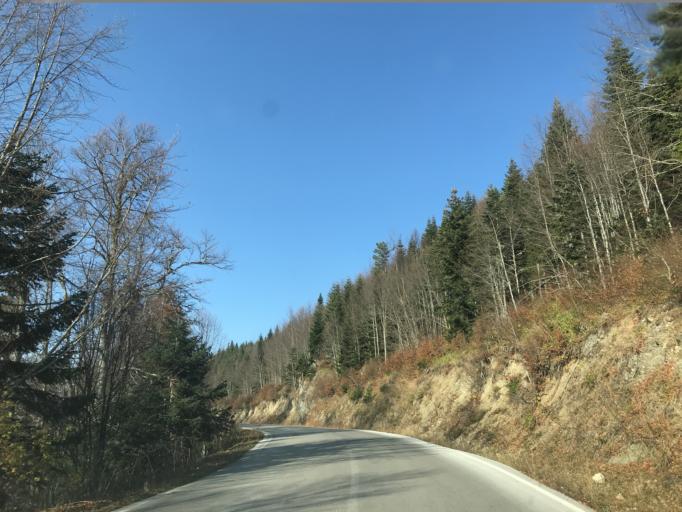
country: TR
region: Bolu
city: Bolu
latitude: 40.8902
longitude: 31.6758
